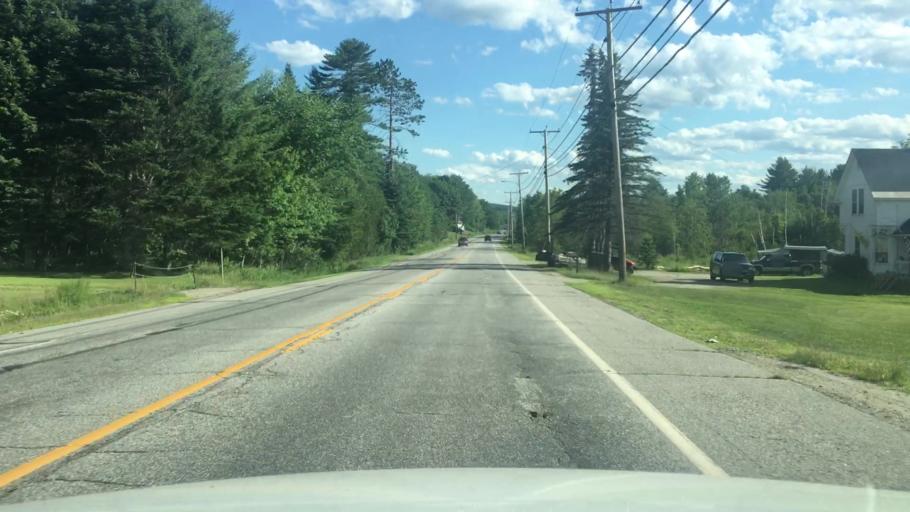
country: US
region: Maine
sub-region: Franklin County
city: Wilton
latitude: 44.5546
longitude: -70.2365
